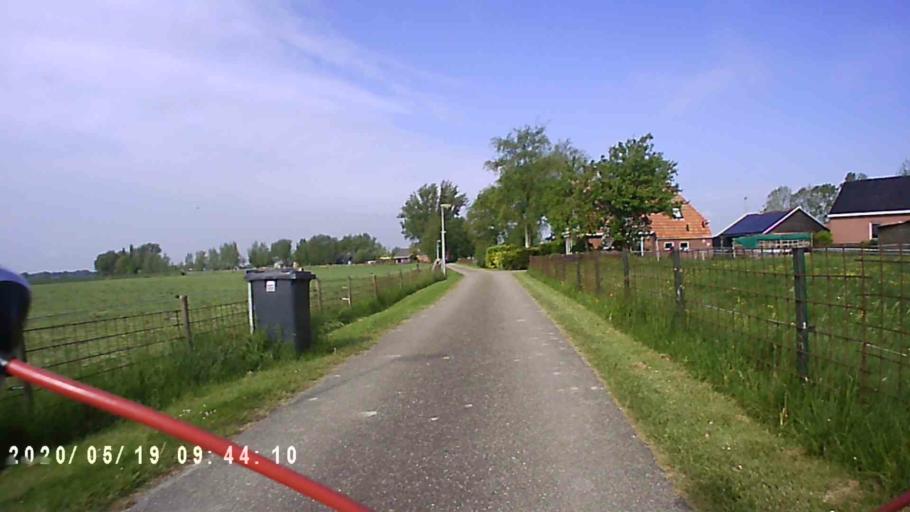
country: NL
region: Groningen
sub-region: Gemeente Zuidhorn
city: Grijpskerk
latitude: 53.2794
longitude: 6.2707
